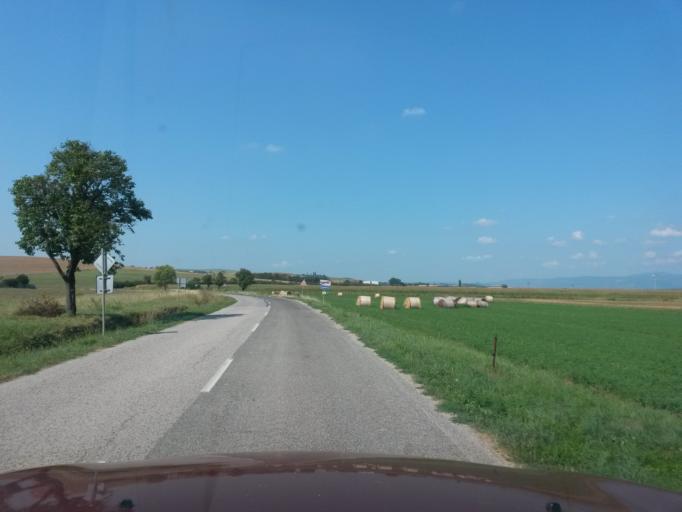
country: SK
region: Kosicky
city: Moldava nad Bodvou
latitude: 48.5325
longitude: 21.1095
